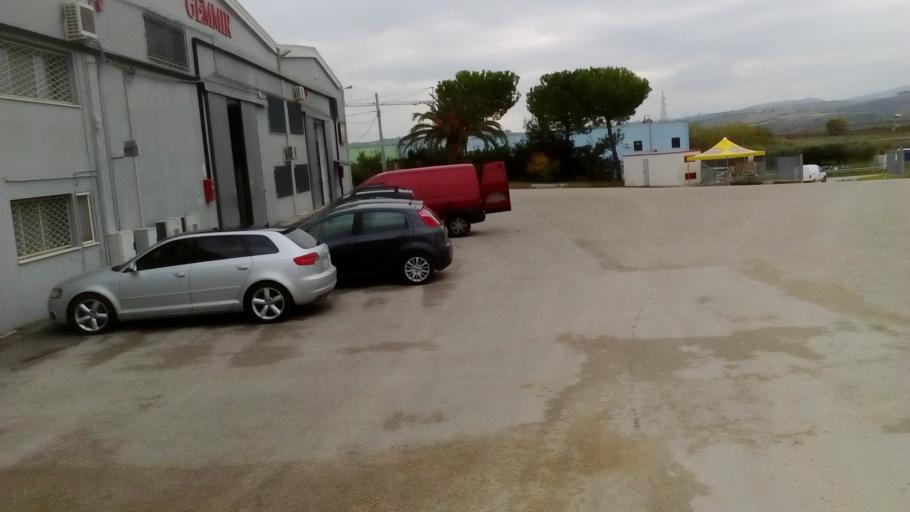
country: IT
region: Abruzzo
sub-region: Provincia di Chieti
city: San Salvo
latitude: 42.0282
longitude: 14.7370
